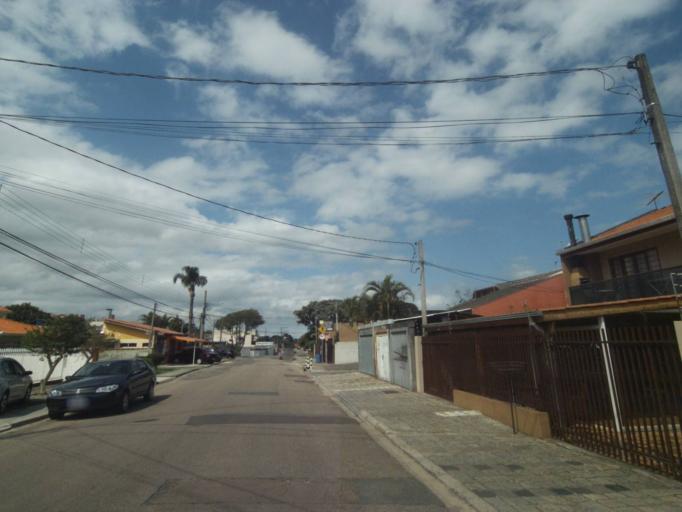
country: BR
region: Parana
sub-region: Pinhais
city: Pinhais
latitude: -25.4107
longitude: -49.2017
